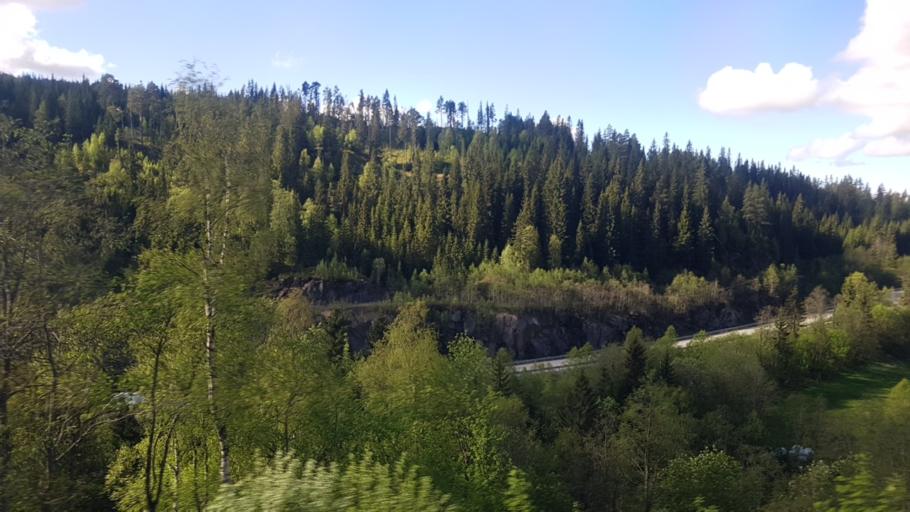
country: NO
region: Sor-Trondelag
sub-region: Midtre Gauldal
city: Storen
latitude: 62.9968
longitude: 10.2375
